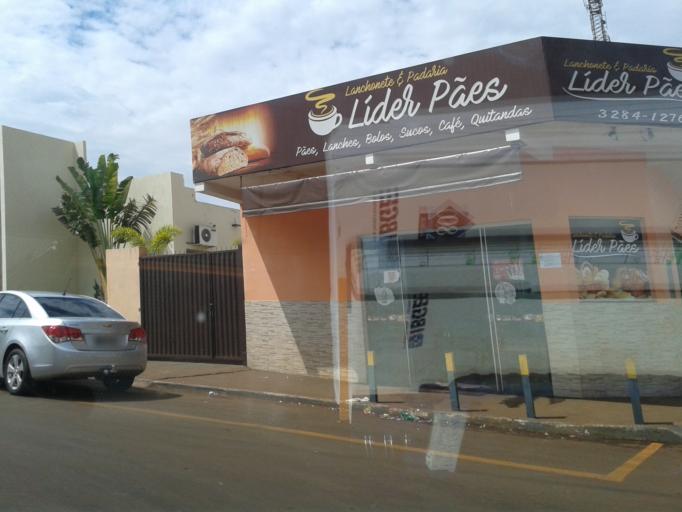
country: BR
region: Goias
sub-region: Itumbiara
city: Itumbiara
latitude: -18.4321
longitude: -49.1881
